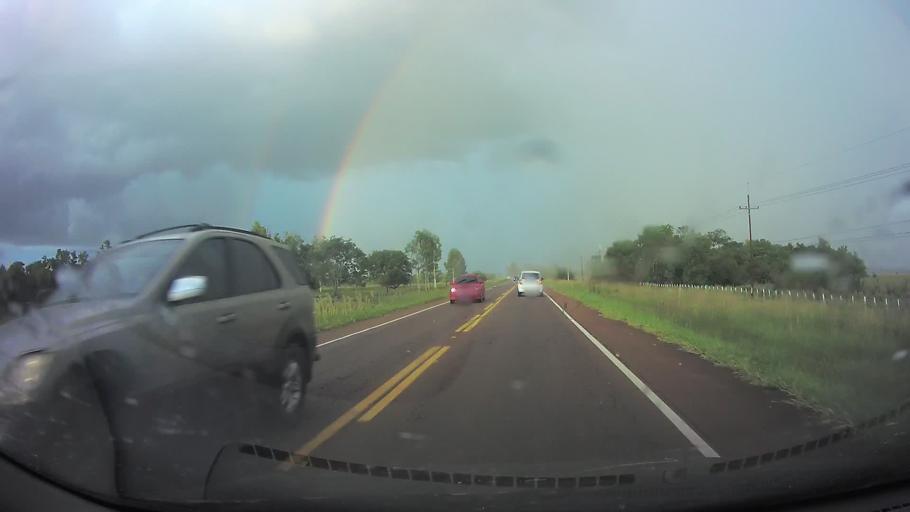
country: PY
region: Paraguari
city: Carapegua
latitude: -25.7110
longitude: -57.1899
